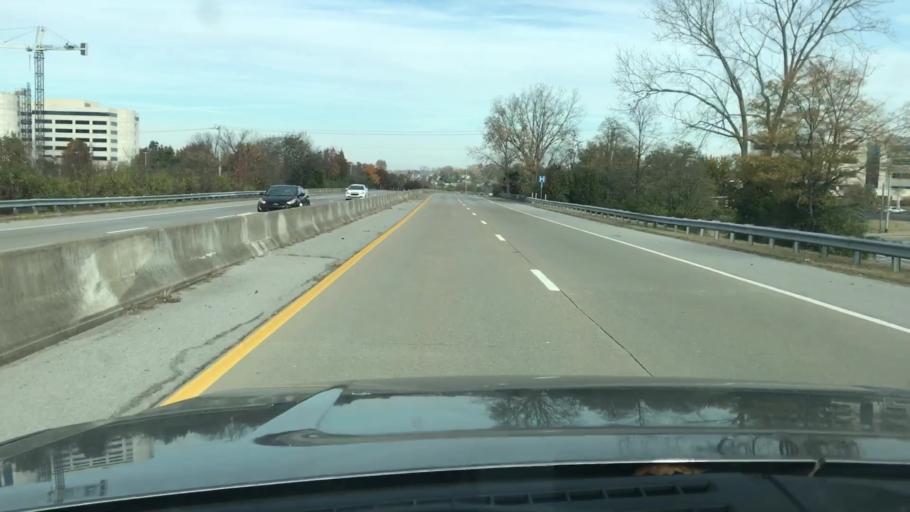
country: US
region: Tennessee
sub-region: Wilson County
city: Green Hill
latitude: 36.1731
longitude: -86.6060
